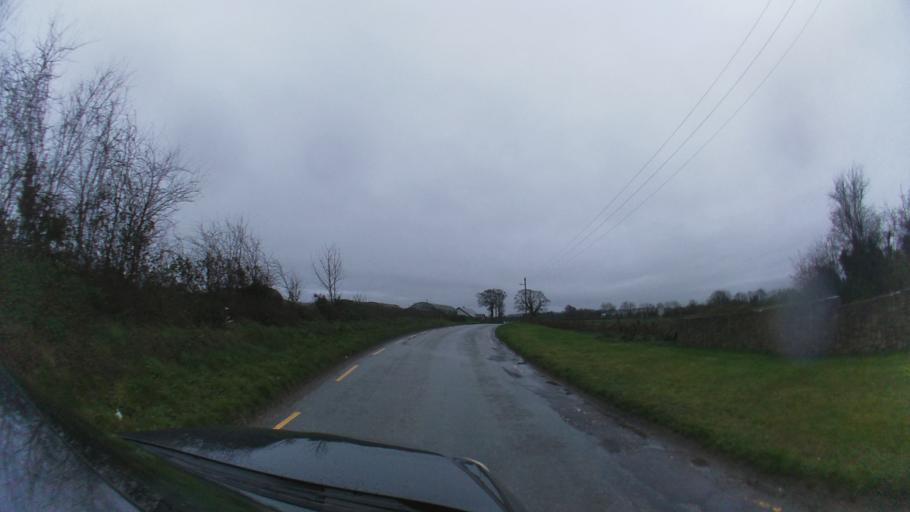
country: IE
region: Leinster
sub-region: County Carlow
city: Bagenalstown
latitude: 52.6273
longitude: -6.9926
